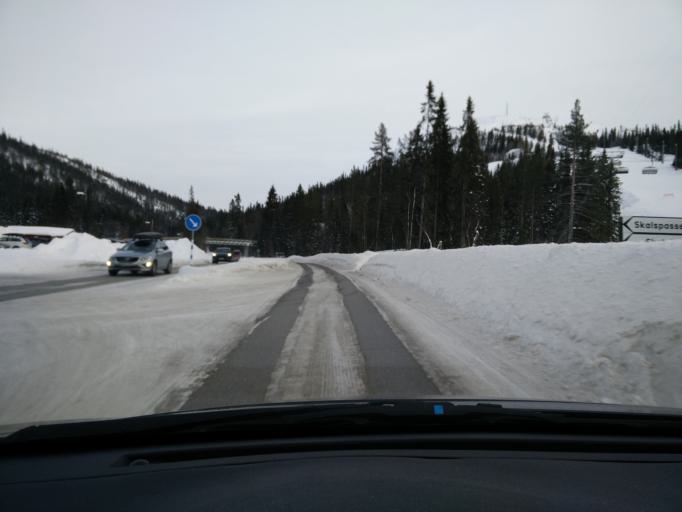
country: SE
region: Jaemtland
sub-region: Bergs Kommun
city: Hoverberg
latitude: 62.4924
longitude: 13.9423
